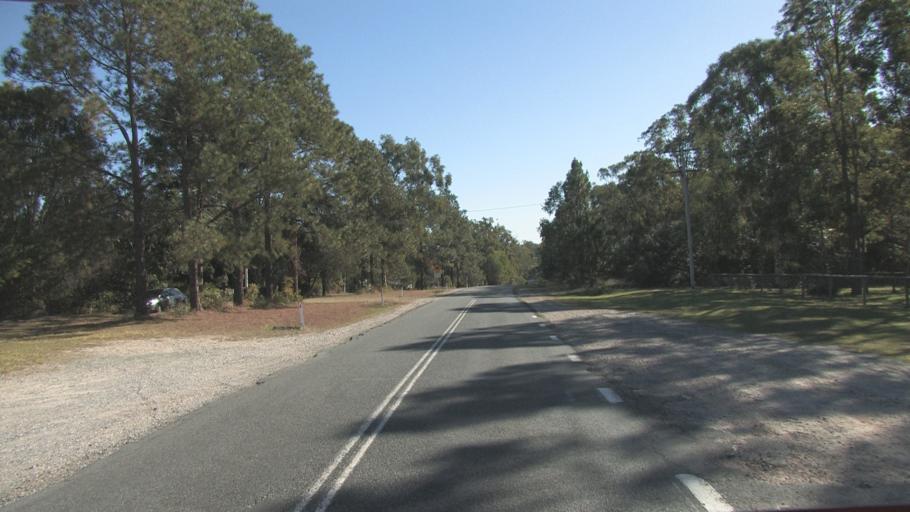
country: AU
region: Queensland
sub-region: Logan
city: Chambers Flat
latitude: -27.7767
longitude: 153.0874
